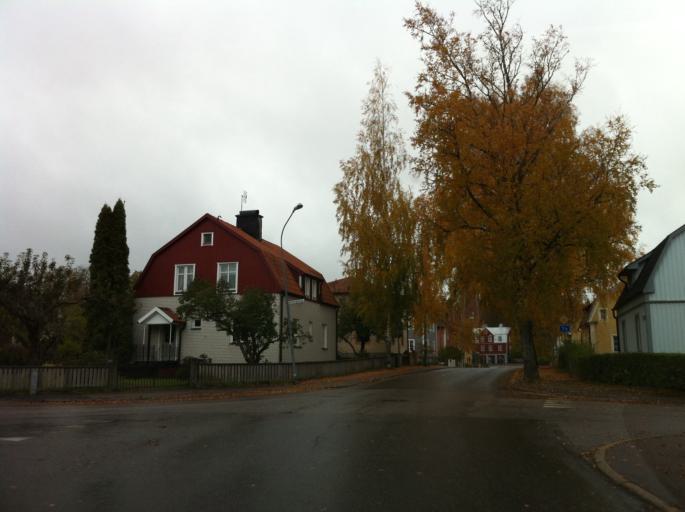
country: SE
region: Uppsala
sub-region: Osthammars Kommun
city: OEsthammar
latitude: 60.2606
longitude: 18.3701
